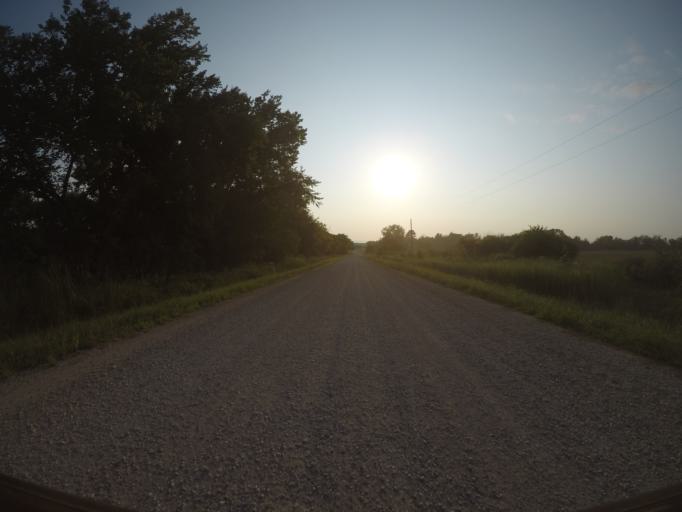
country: US
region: Kansas
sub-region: Pottawatomie County
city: Wamego
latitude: 39.1086
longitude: -96.4161
